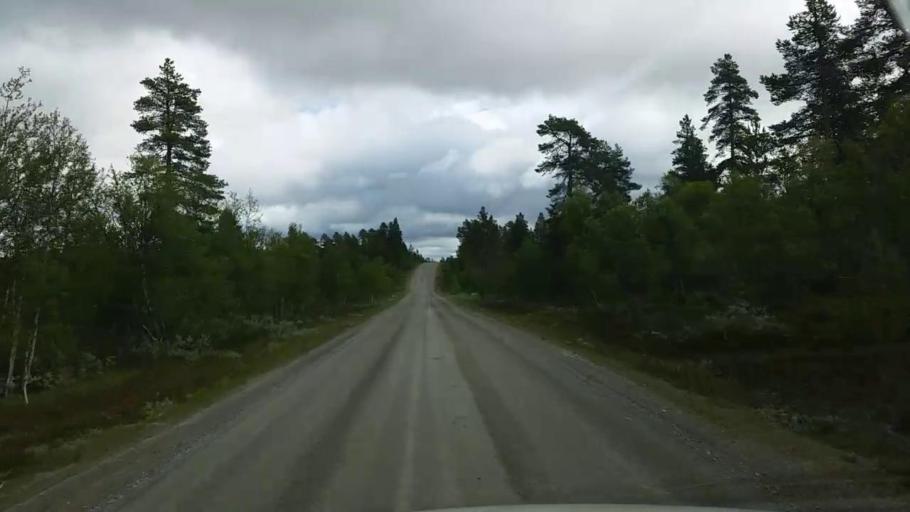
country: NO
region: Hedmark
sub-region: Engerdal
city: Engerdal
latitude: 62.3471
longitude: 12.5890
